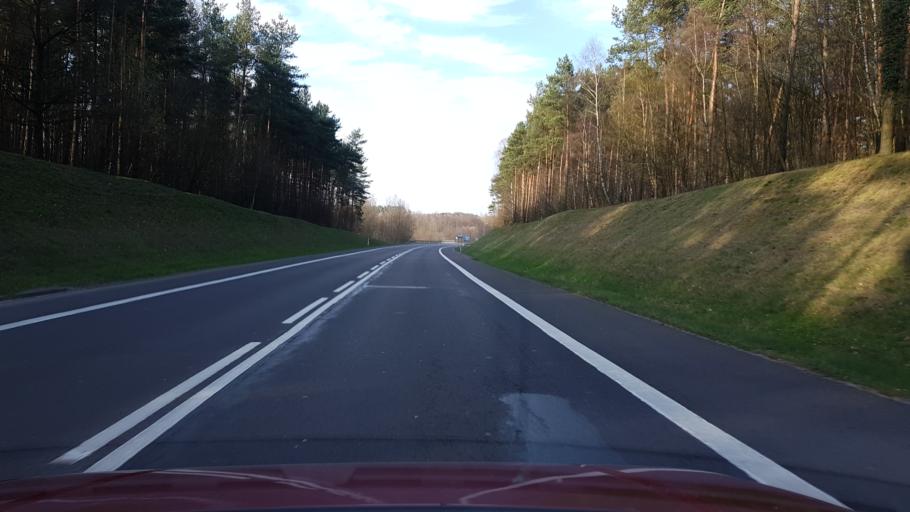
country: PL
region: West Pomeranian Voivodeship
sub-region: Powiat bialogardzki
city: Karlino
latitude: 54.0423
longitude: 15.8983
